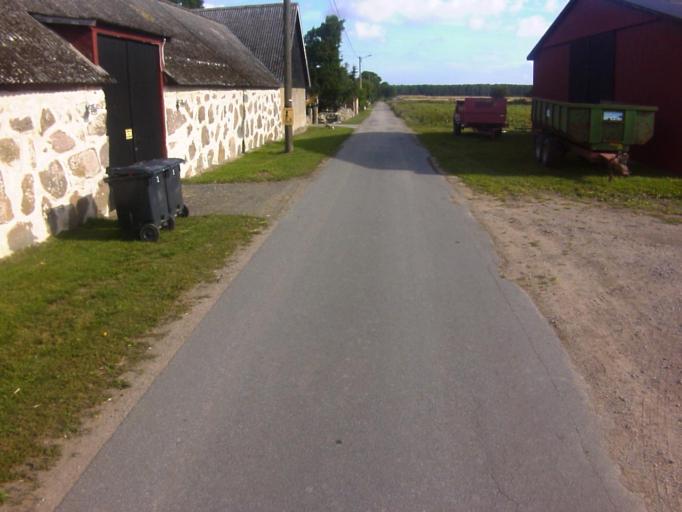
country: SE
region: Blekinge
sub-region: Solvesborgs Kommun
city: Soelvesborg
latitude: 56.0432
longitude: 14.7118
